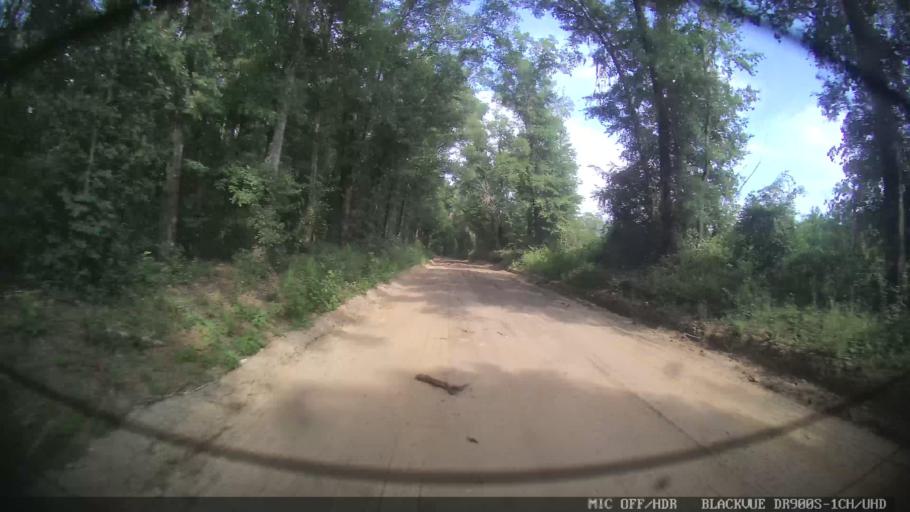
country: US
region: Georgia
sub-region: Lowndes County
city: Valdosta
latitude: 30.6194
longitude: -83.2387
